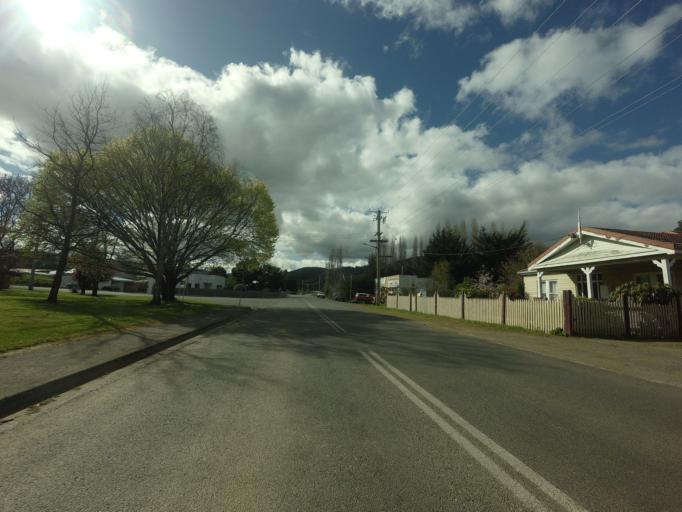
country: AU
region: Tasmania
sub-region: Huon Valley
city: Geeveston
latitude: -43.1682
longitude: 146.9261
